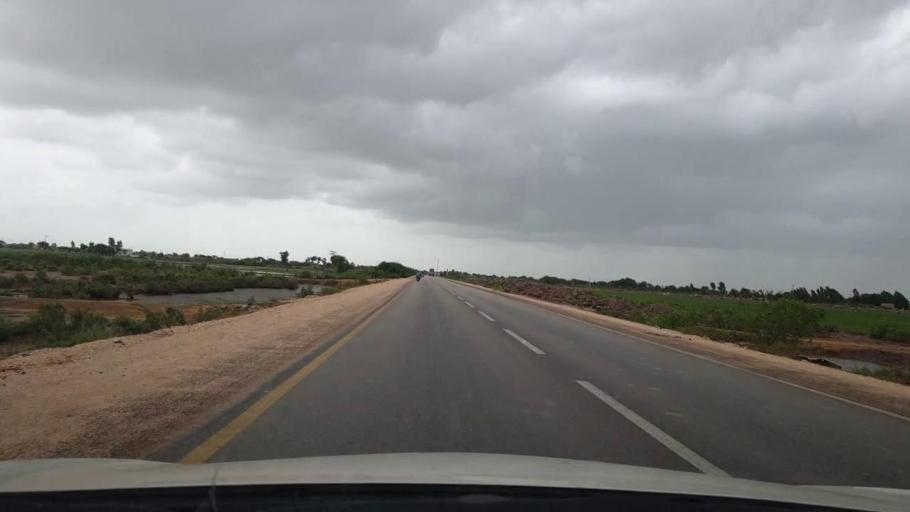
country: PK
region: Sindh
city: Mirpur Batoro
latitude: 24.6431
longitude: 68.4467
